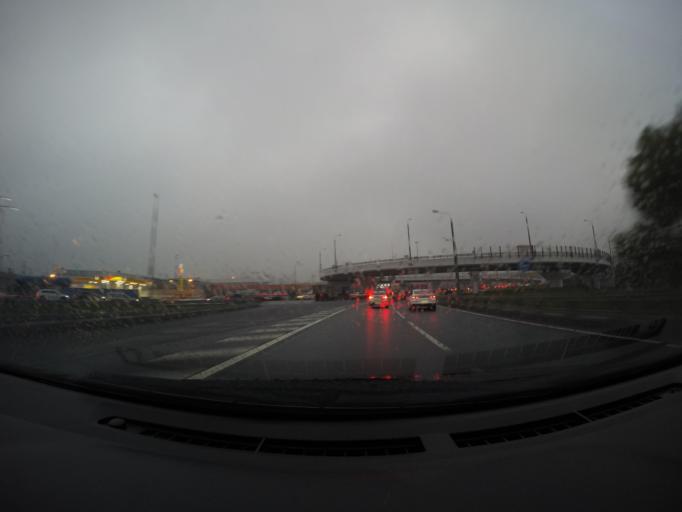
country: RU
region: Moscow
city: Annino
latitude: 55.5777
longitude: 37.5984
